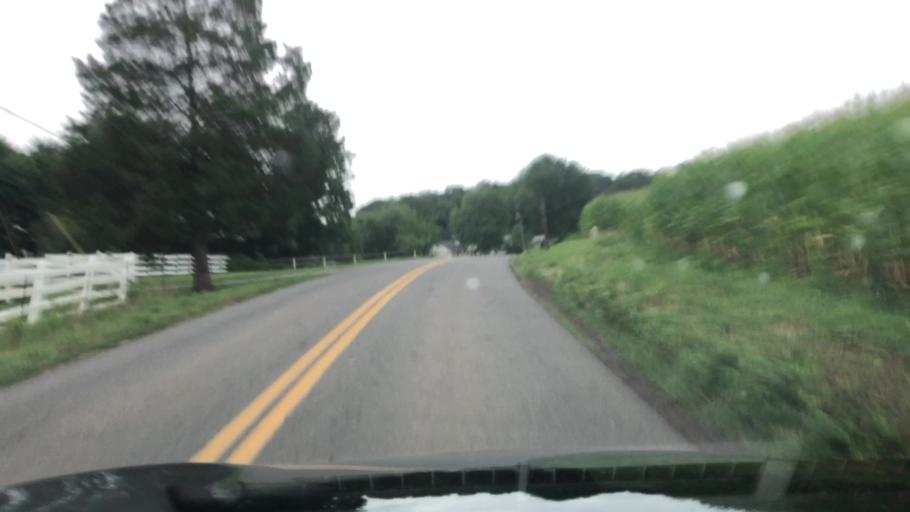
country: US
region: Virginia
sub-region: Prince William County
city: Nokesville
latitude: 38.6686
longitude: -77.6474
